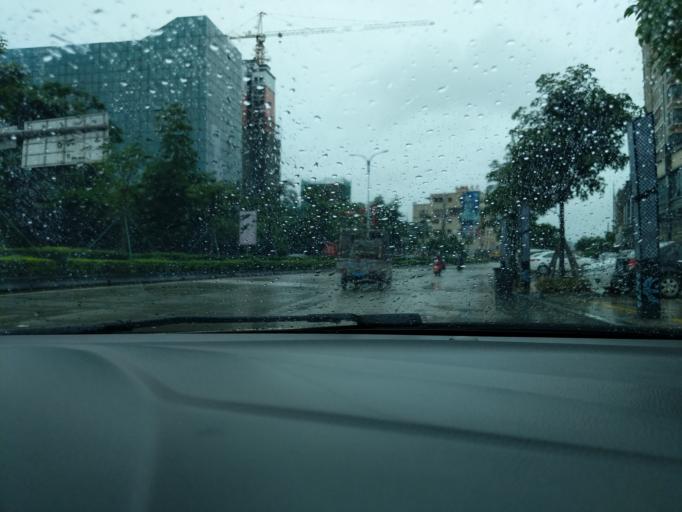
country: CN
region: Guangdong
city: Pingshi
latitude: 22.2031
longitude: 112.3268
